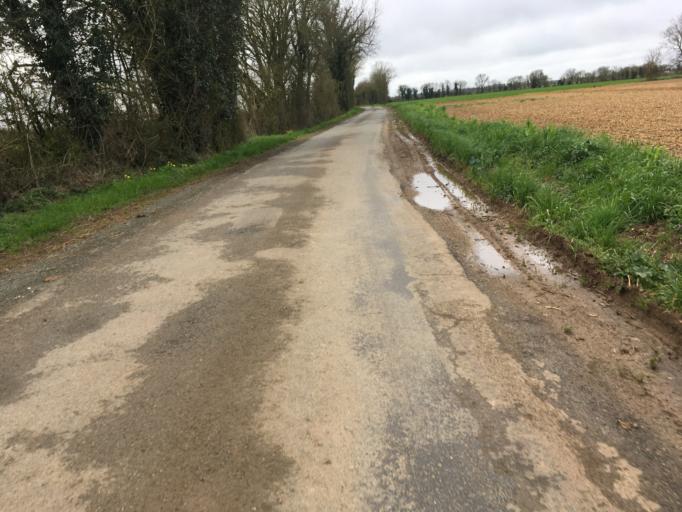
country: FR
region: Poitou-Charentes
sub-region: Departement de la Charente-Maritime
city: Saint-Germain-de-Marencennes
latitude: 46.1131
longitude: -0.8127
